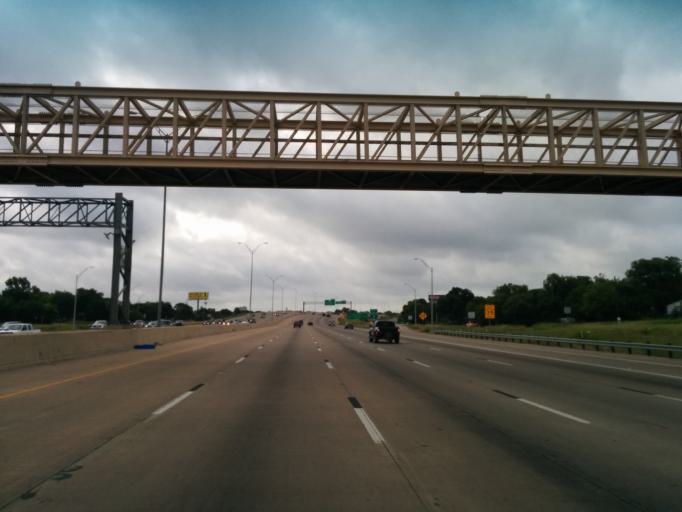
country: US
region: Texas
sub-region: Bexar County
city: Balcones Heights
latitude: 29.4775
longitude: -98.5210
